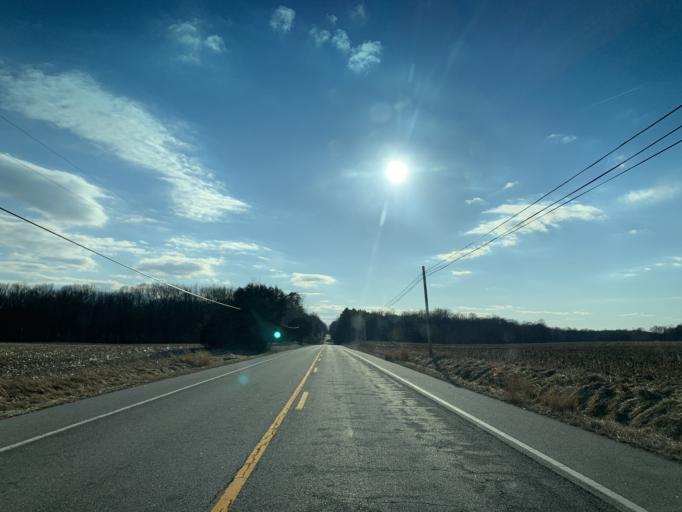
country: US
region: Maryland
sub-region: Queen Anne's County
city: Kingstown
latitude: 39.1575
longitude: -75.9515
